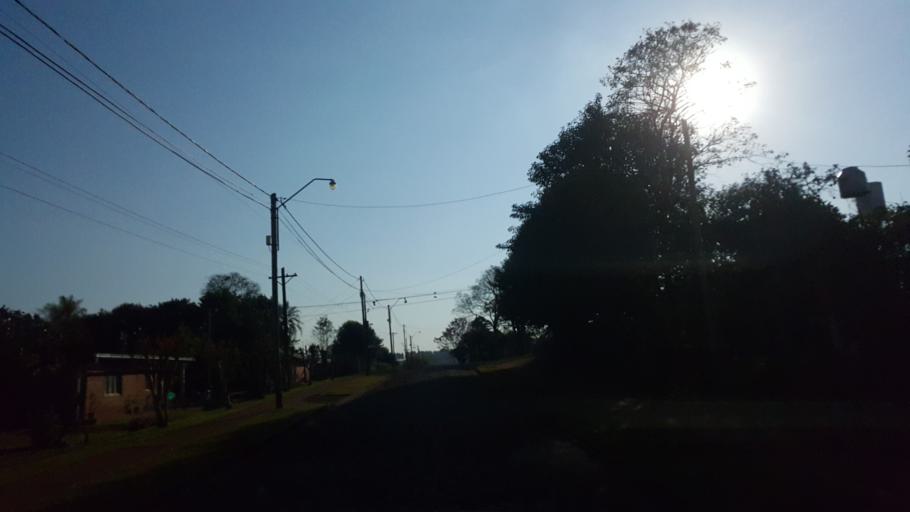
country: AR
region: Misiones
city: Capiovi
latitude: -26.8912
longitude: -55.0718
